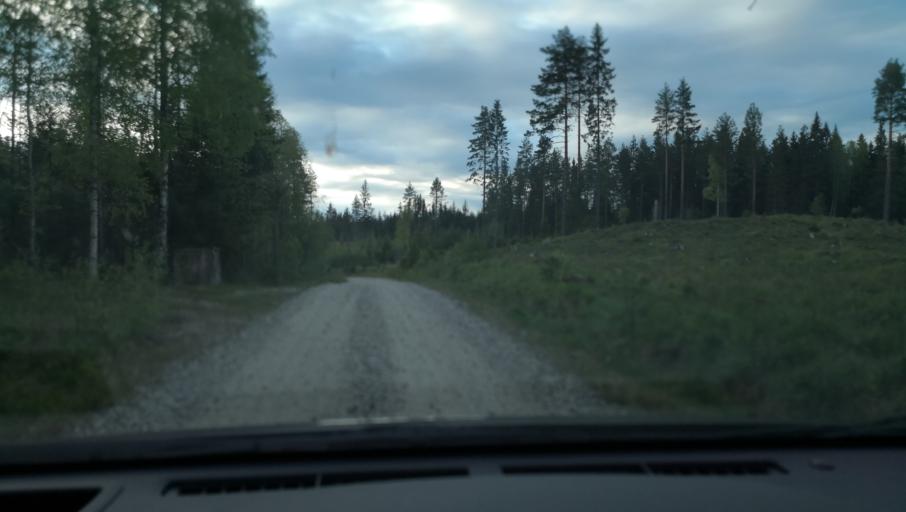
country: SE
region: Vaestmanland
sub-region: Skinnskattebergs Kommun
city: Skinnskatteberg
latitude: 59.7976
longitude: 15.4620
